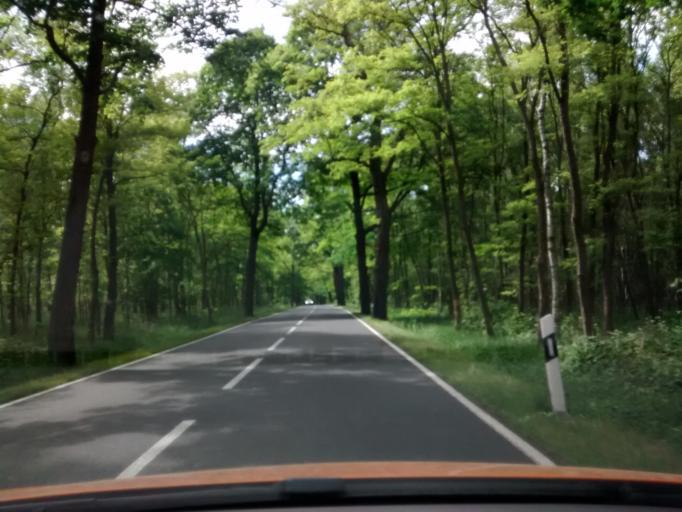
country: DE
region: Brandenburg
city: Ihlow
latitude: 51.9877
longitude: 13.2859
